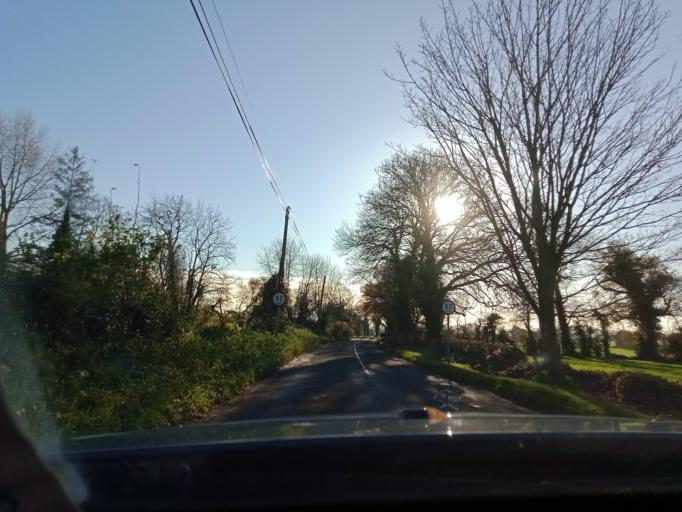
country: IE
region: Leinster
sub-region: Kilkenny
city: Piltown
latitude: 52.3837
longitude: -7.3436
